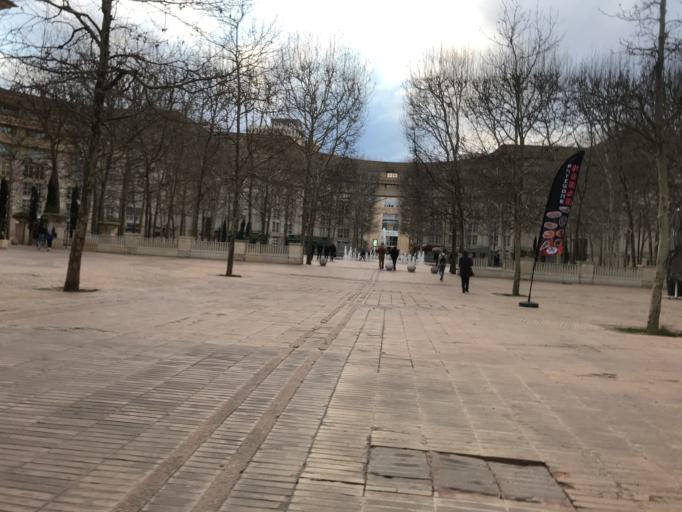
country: FR
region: Languedoc-Roussillon
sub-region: Departement de l'Herault
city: Montpellier
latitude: 43.6081
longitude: 3.8885
